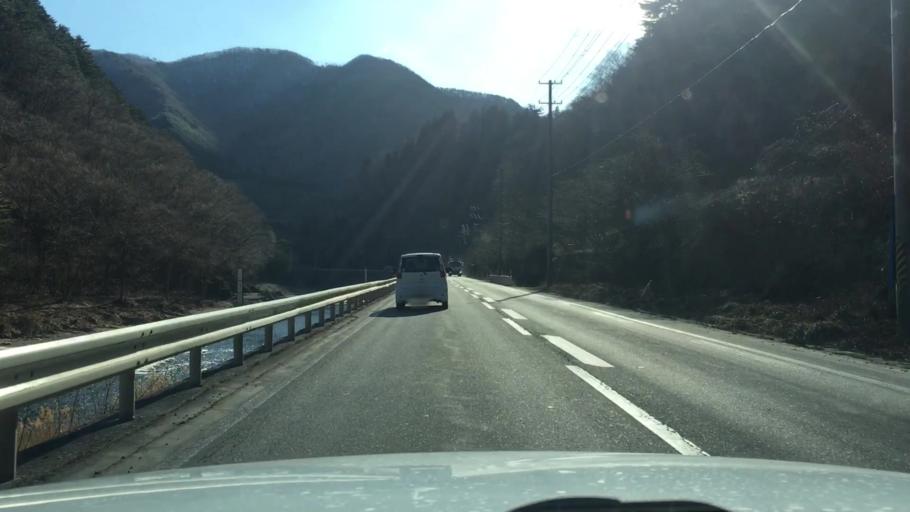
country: JP
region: Iwate
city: Miyako
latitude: 39.6093
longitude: 141.7733
